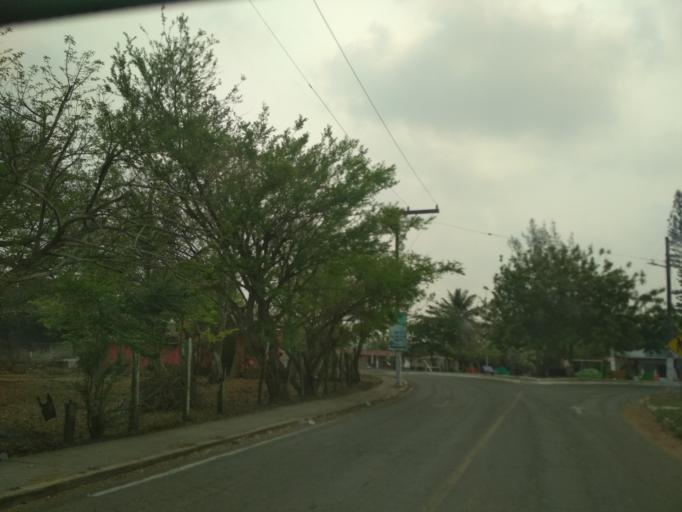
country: MX
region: Veracruz
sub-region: Veracruz
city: Fraccionamiento Geovillas los Pinos
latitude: 19.2104
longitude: -96.2484
